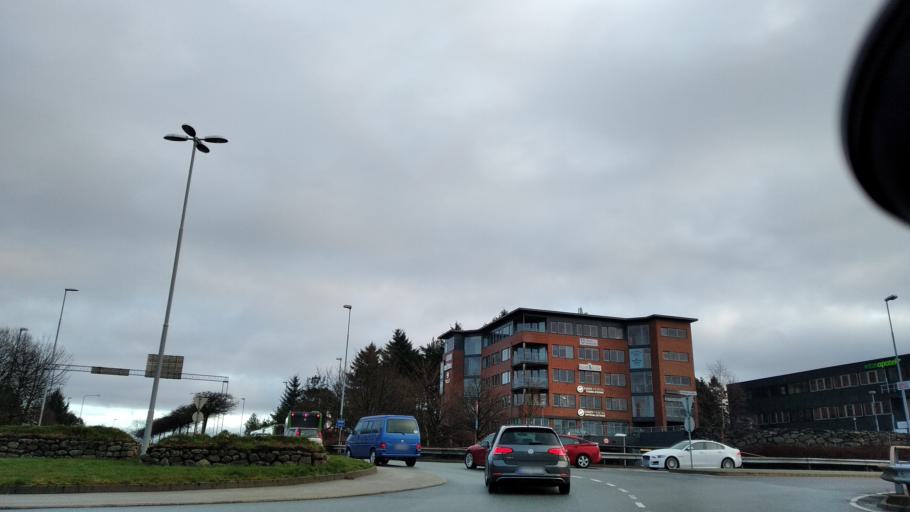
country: NO
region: Rogaland
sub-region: Stavanger
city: Stavanger
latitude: 58.9531
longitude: 5.6817
